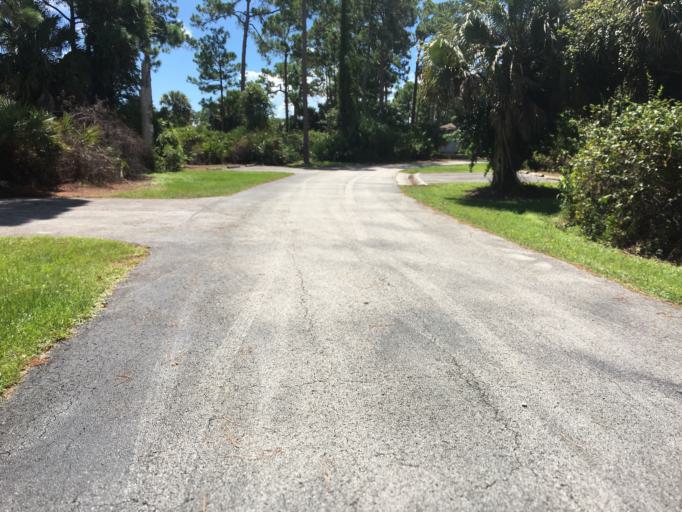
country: US
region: Florida
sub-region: Martin County
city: Stuart
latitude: 27.1881
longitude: -80.2711
